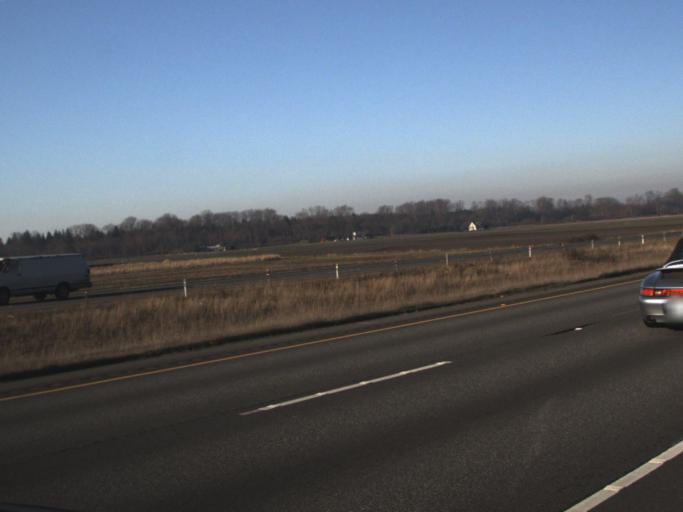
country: US
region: Washington
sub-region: Snohomish County
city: Stanwood
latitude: 48.3256
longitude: -122.3299
